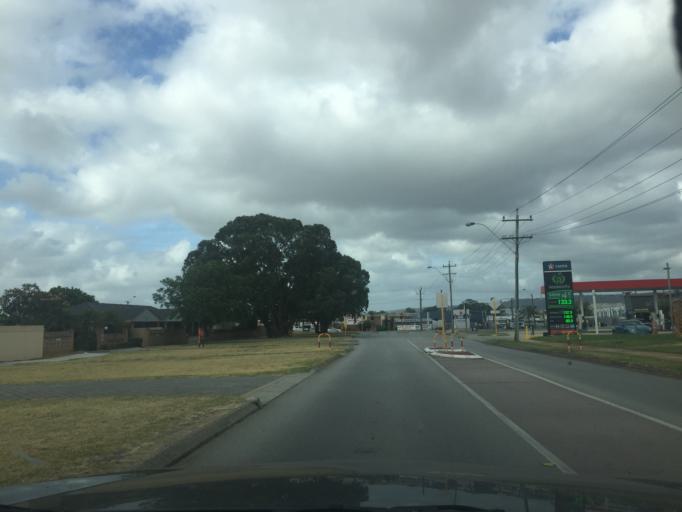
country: AU
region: Western Australia
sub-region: Gosnells
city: Maddington
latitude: -32.0496
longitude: 115.9767
